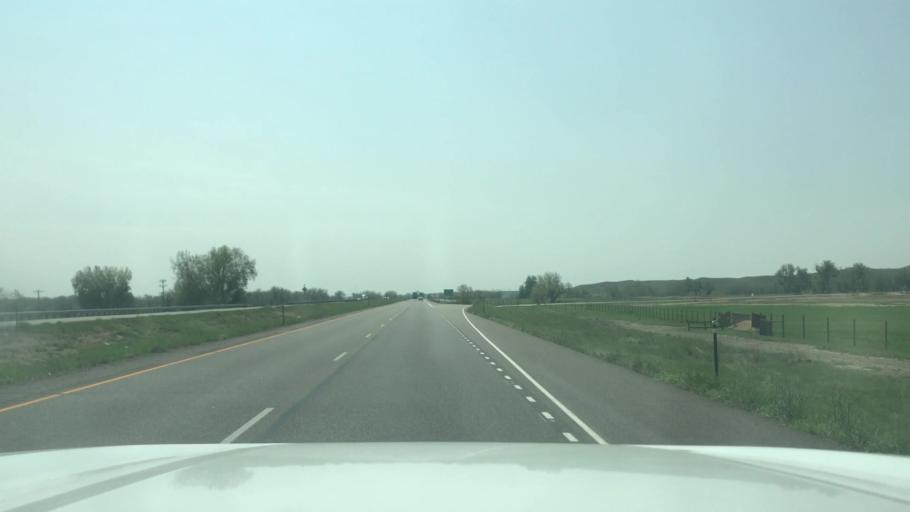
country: US
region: Colorado
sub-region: El Paso County
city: Fountain
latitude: 38.6316
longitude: -104.6915
